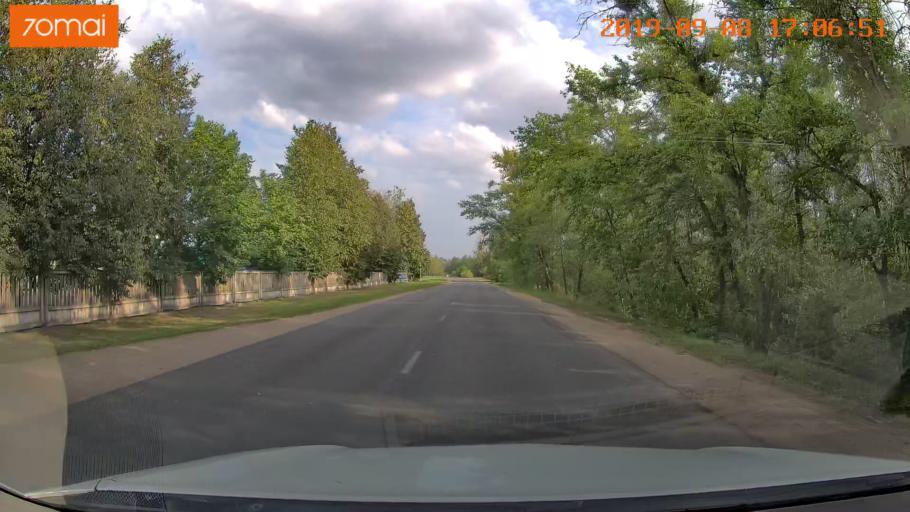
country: BY
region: Grodnenskaya
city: Hrodna
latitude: 53.6674
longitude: 23.9533
